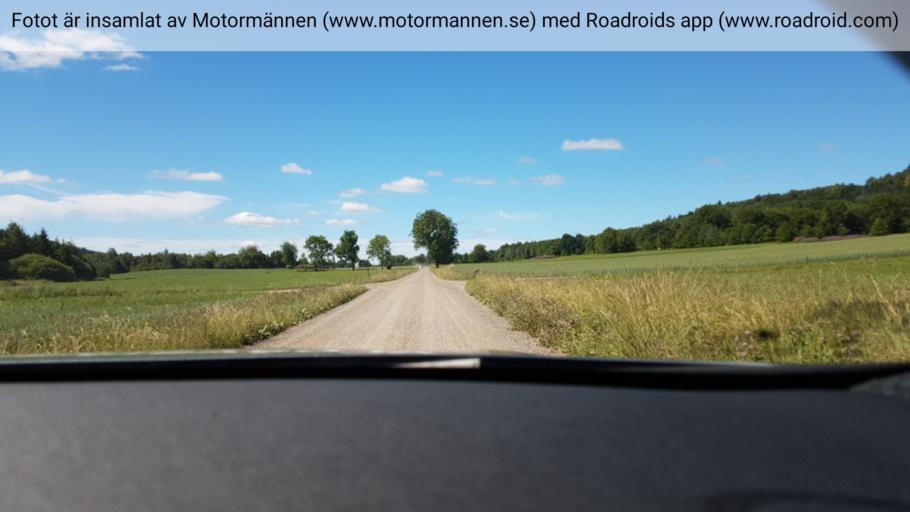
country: SE
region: Vaestra Goetaland
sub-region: Falkopings Kommun
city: Akarp
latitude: 58.2217
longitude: 13.7715
